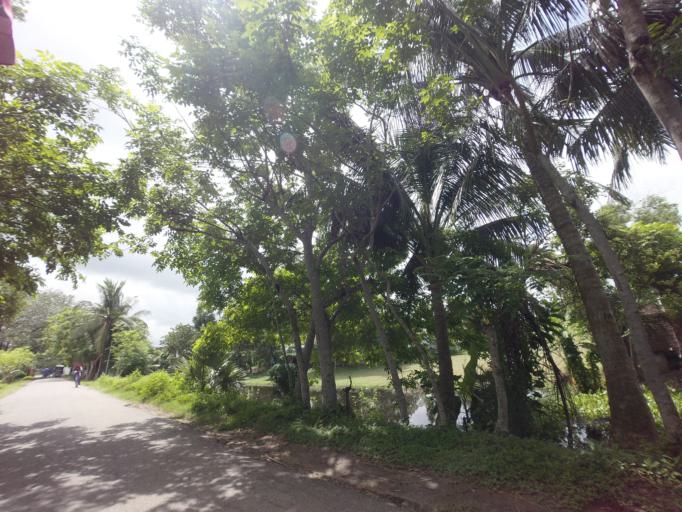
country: BD
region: Khulna
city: Kalia
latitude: 23.0399
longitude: 89.6404
